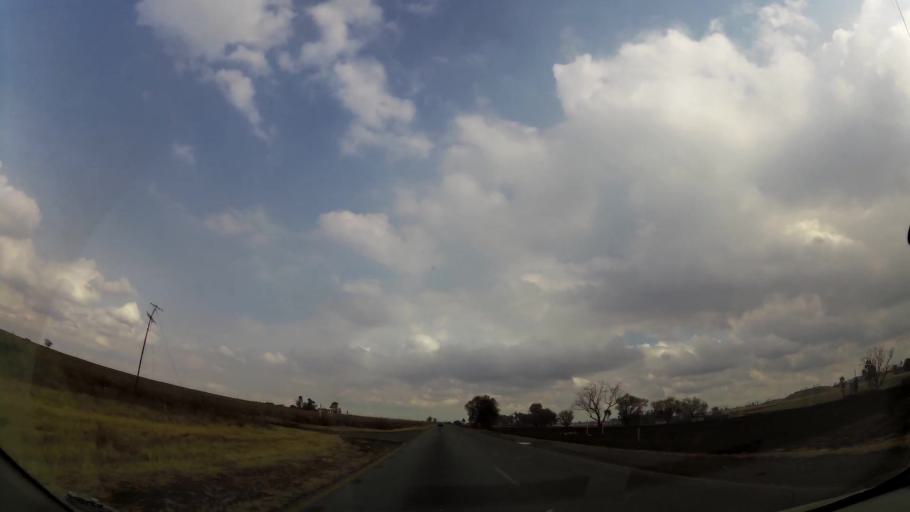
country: ZA
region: Orange Free State
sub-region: Fezile Dabi District Municipality
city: Sasolburg
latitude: -26.8280
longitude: 27.9002
